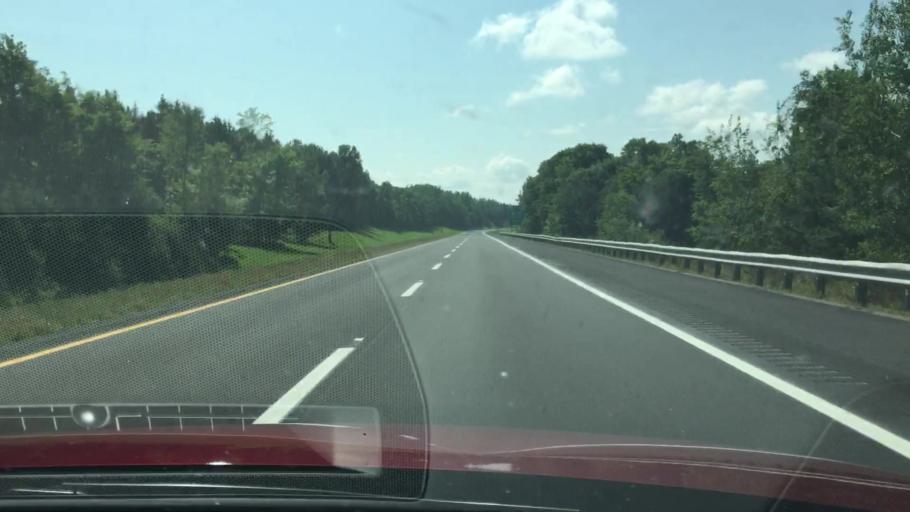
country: US
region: Maine
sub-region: Penobscot County
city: Patten
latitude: 45.9098
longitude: -68.3806
